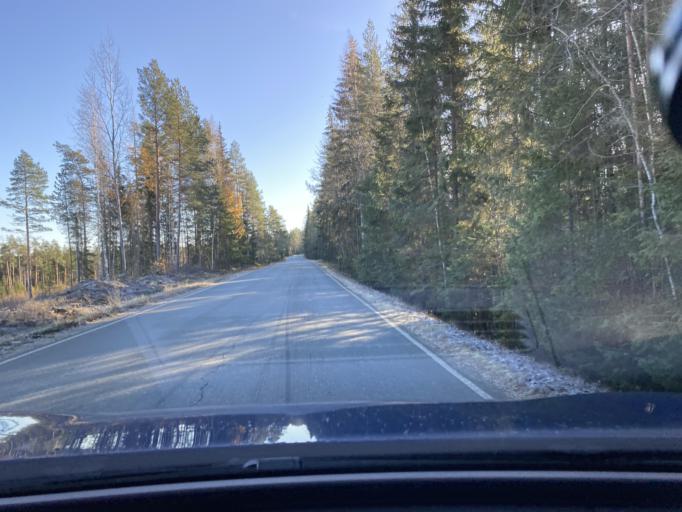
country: FI
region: Pirkanmaa
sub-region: Etelae-Pirkanmaa
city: Kylmaekoski
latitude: 61.0605
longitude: 23.6713
